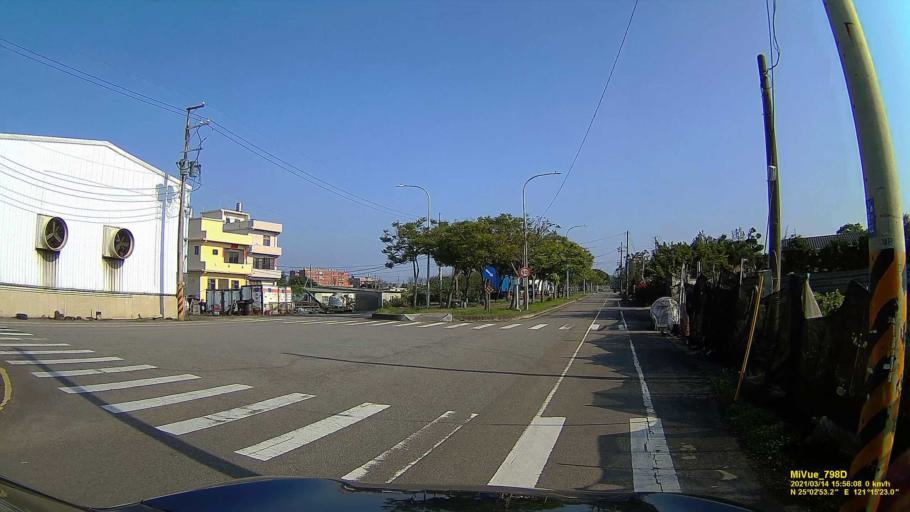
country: TW
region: Taiwan
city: Taoyuan City
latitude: 25.0481
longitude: 121.2564
